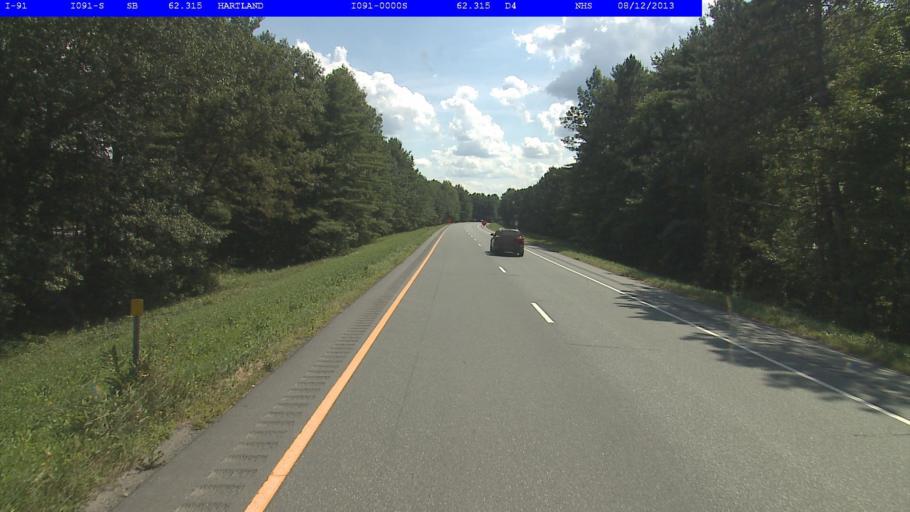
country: US
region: Vermont
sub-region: Windsor County
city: Windsor
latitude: 43.5508
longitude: -72.3854
